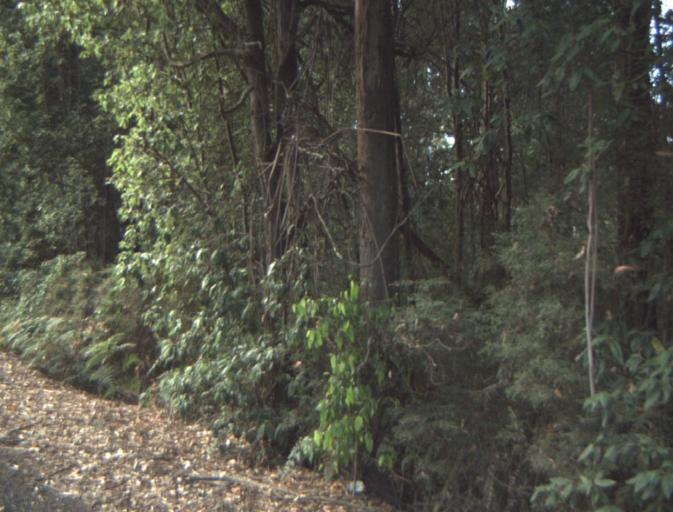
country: AU
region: Tasmania
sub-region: Launceston
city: Mayfield
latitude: -41.2757
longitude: 147.1870
